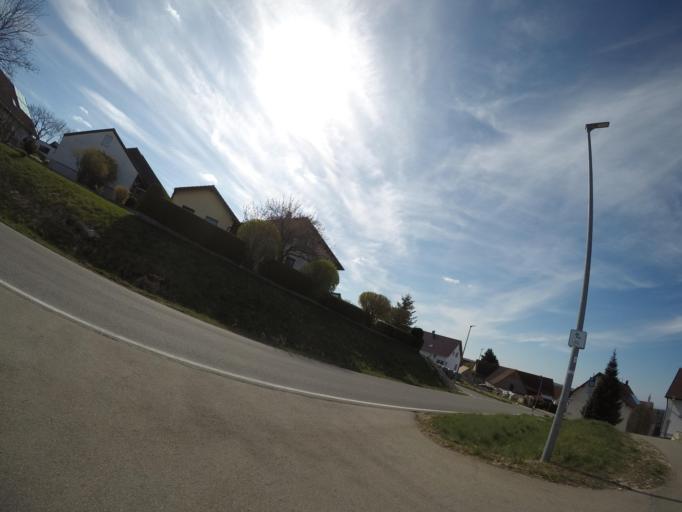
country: DE
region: Baden-Wuerttemberg
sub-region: Tuebingen Region
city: Mehrstetten
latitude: 48.3334
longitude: 9.6014
